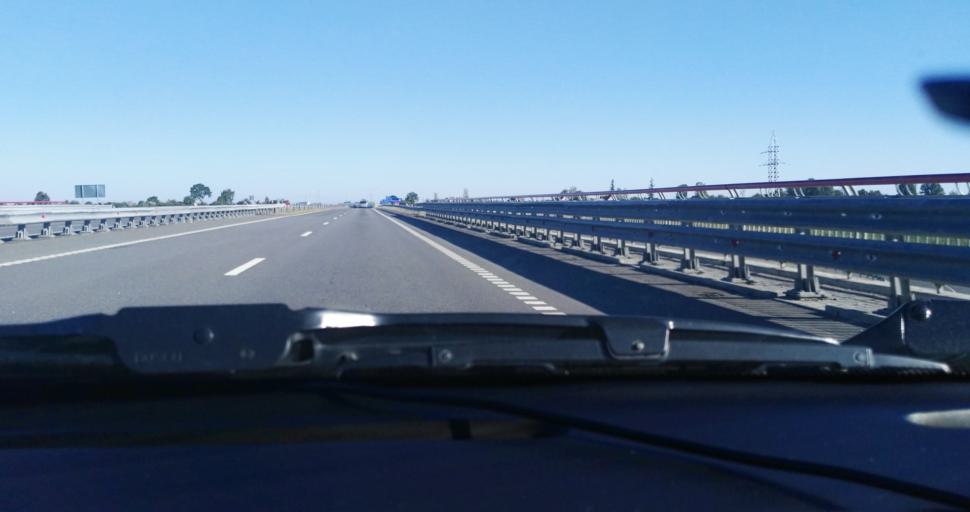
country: BY
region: Gomel
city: Buda-Kashalyova
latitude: 52.5143
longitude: 30.6293
